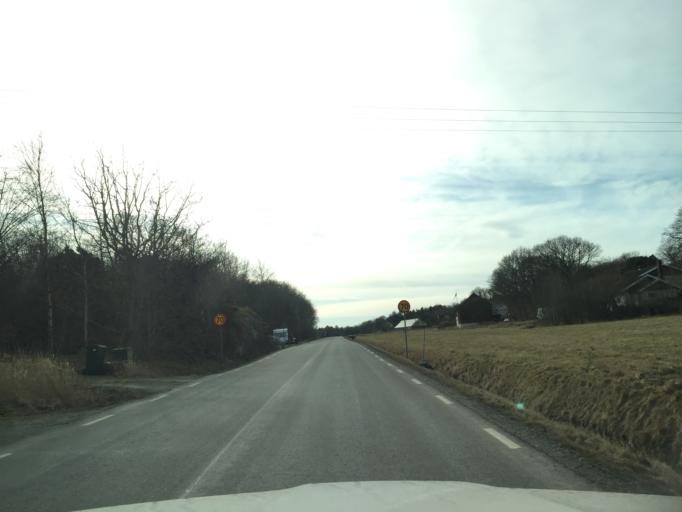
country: SE
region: Vaestra Goetaland
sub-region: Tjorns Kommun
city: Skaerhamn
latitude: 58.0338
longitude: 11.5491
